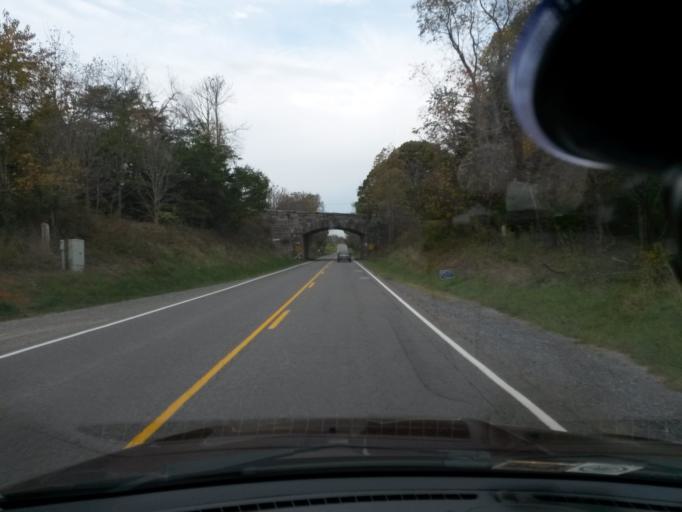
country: US
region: Virginia
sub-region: City of Roanoke
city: Cedar Bluff
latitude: 37.2296
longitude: -79.9049
